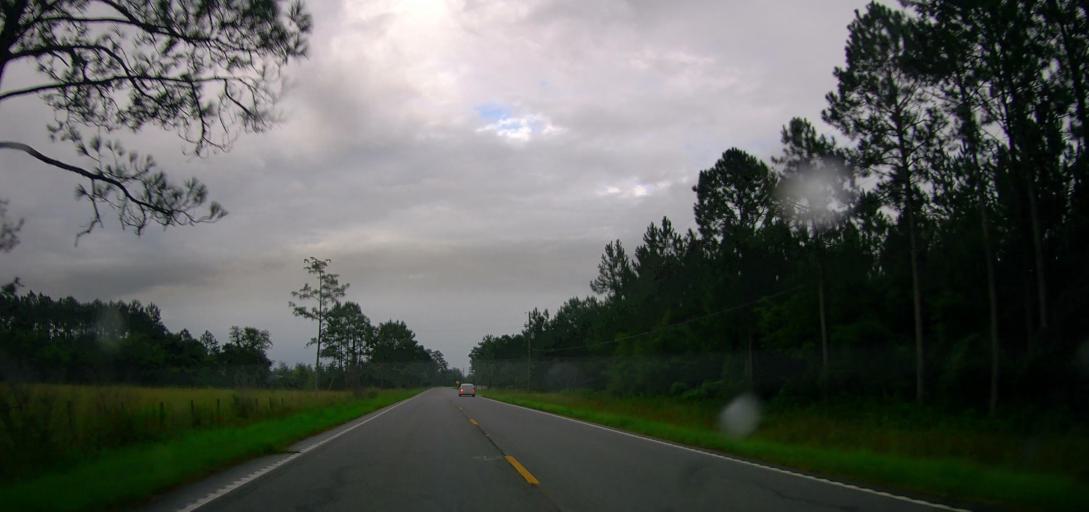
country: US
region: Georgia
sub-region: Ware County
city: Deenwood
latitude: 31.2860
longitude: -82.4365
